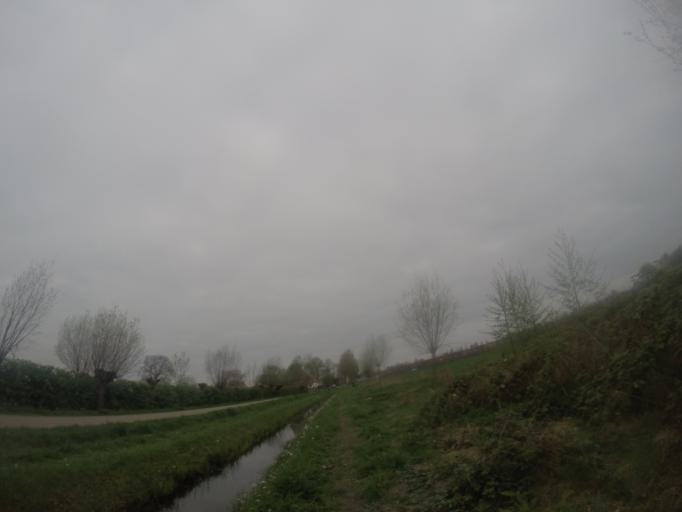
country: NL
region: Gelderland
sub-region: Gemeente Zutphen
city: Leesten
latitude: 52.1213
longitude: 6.2397
